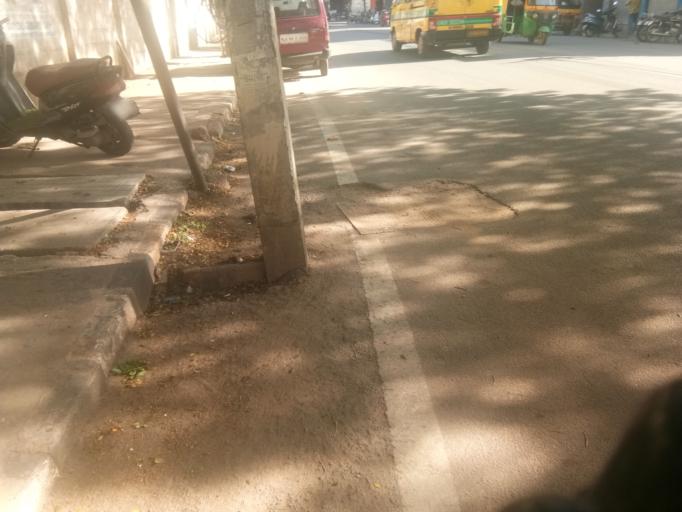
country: IN
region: Karnataka
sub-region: Bangalore Urban
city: Bangalore
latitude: 13.0181
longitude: 77.5983
